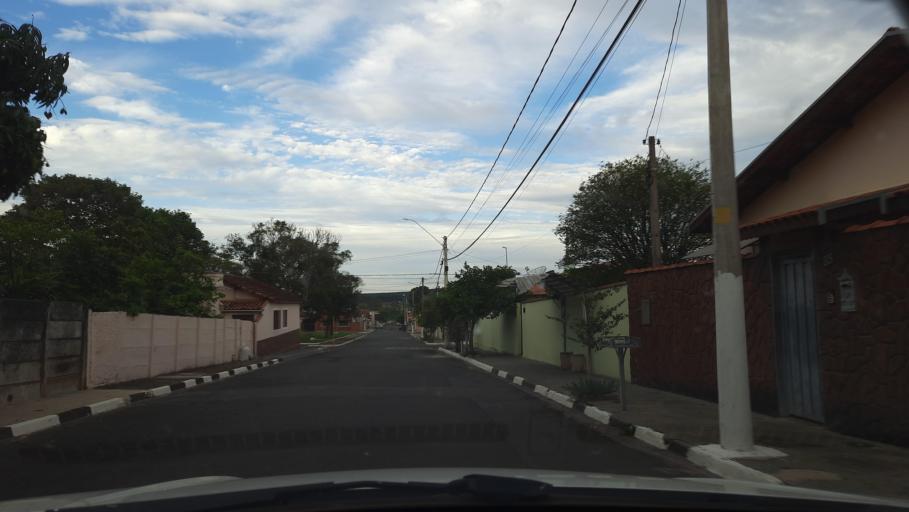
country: BR
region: Sao Paulo
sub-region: Casa Branca
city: Casa Branca
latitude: -21.7819
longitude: -47.0665
